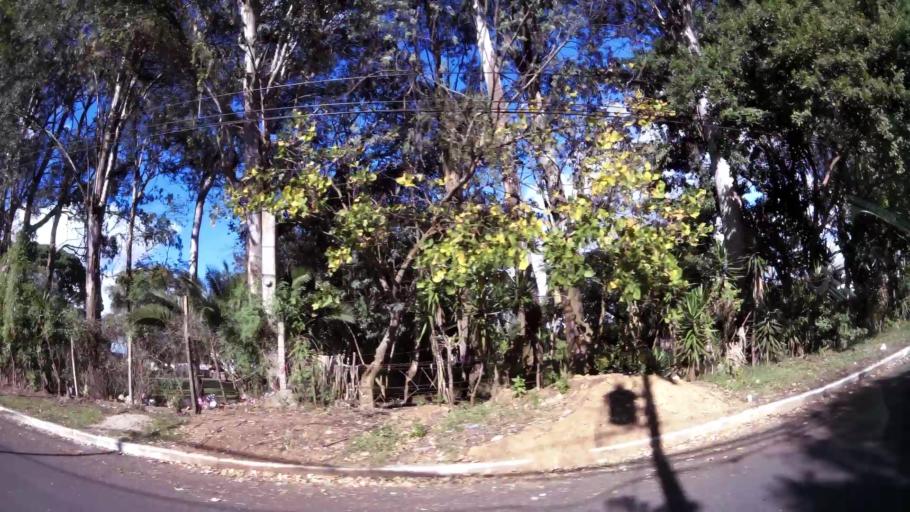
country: GT
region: Guatemala
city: Guatemala City
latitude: 14.6041
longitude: -90.5569
